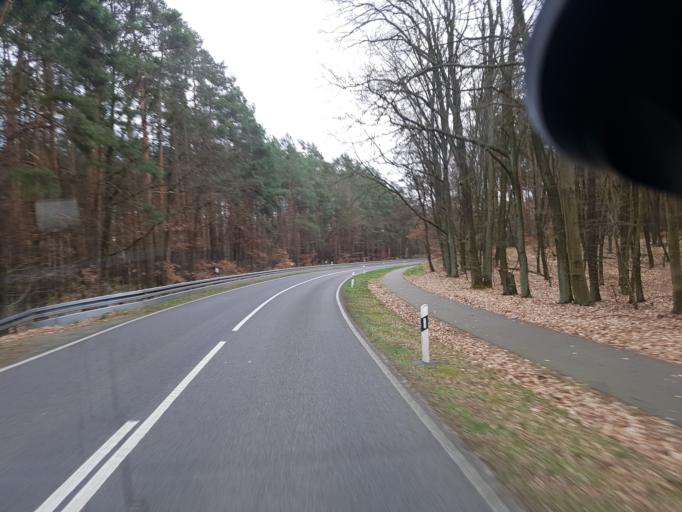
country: DE
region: Brandenburg
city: Mixdorf
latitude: 52.1862
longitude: 14.4724
